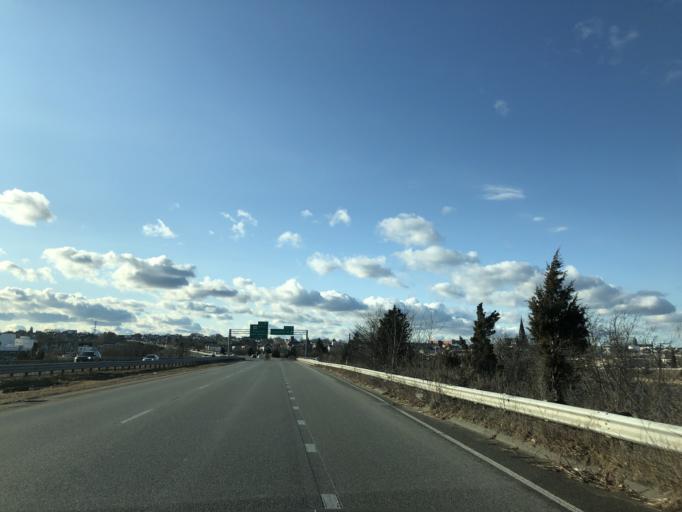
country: US
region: Massachusetts
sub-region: Bristol County
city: Fairhaven
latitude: 41.6547
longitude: -70.9162
